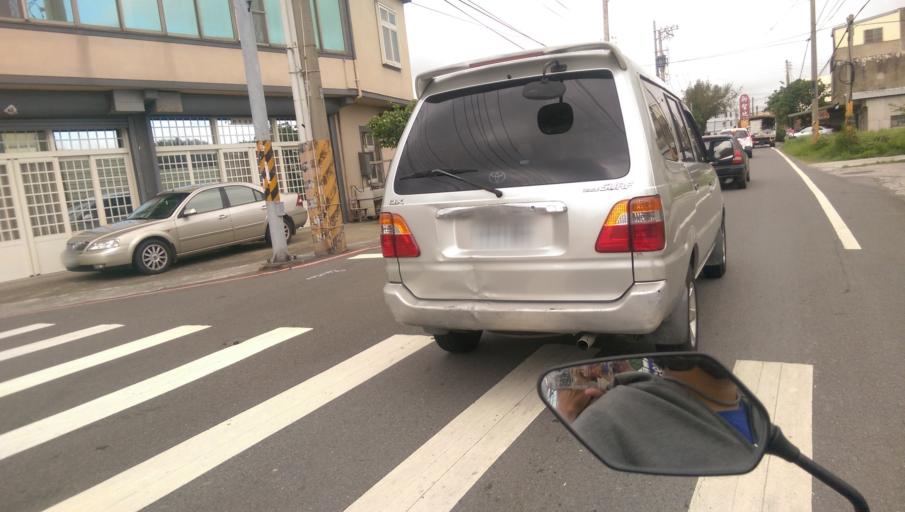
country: TW
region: Taiwan
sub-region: Hsinchu
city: Hsinchu
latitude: 24.8181
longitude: 120.9291
